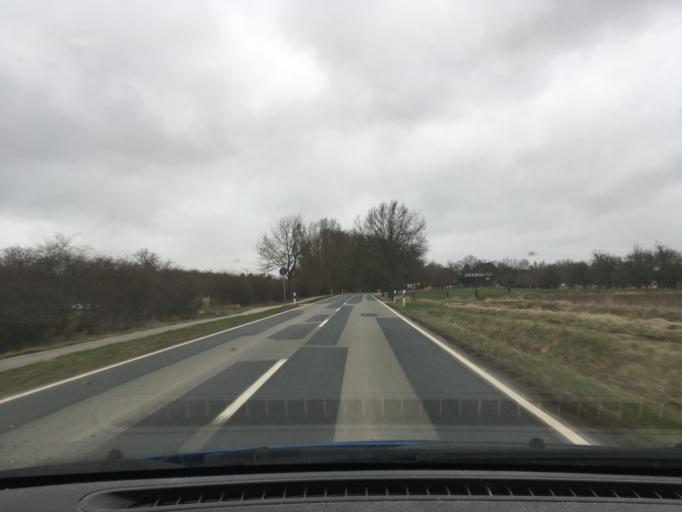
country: DE
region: Lower Saxony
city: Drage
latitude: 53.4036
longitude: 10.2618
